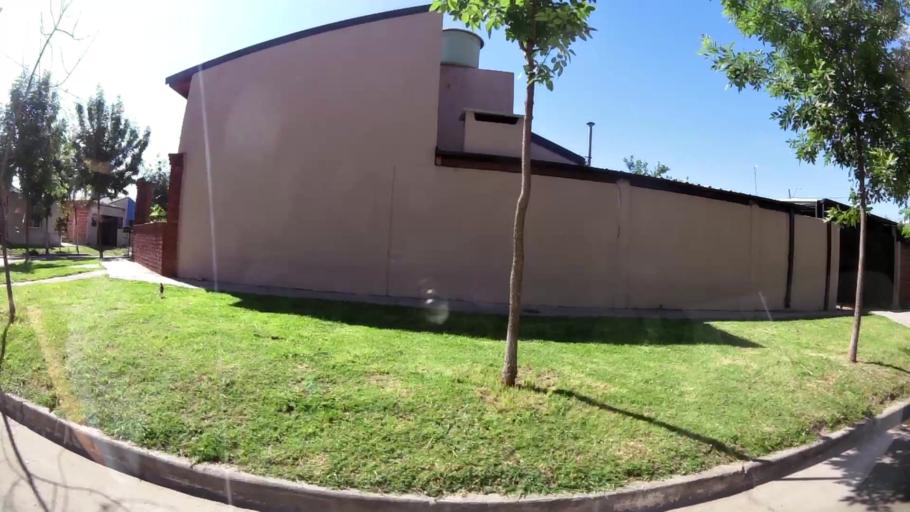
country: AR
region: Buenos Aires
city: Hurlingham
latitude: -34.6208
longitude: -58.6516
